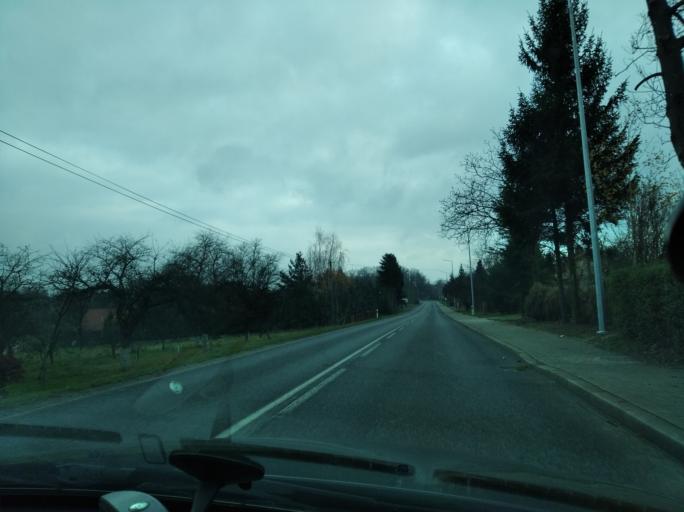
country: PL
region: Subcarpathian Voivodeship
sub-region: Powiat przeworski
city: Sietesz
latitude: 50.0023
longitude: 22.3496
